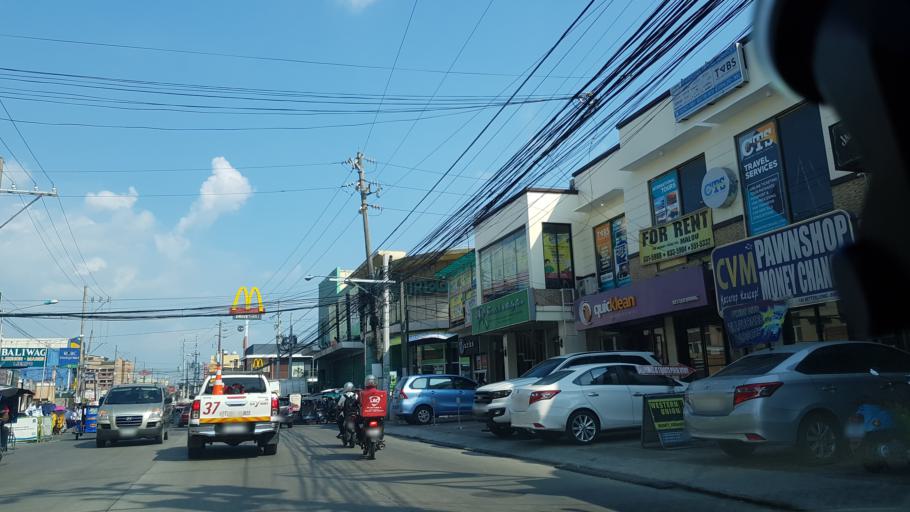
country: PH
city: Sambayanihan People's Village
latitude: 14.4850
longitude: 121.0294
